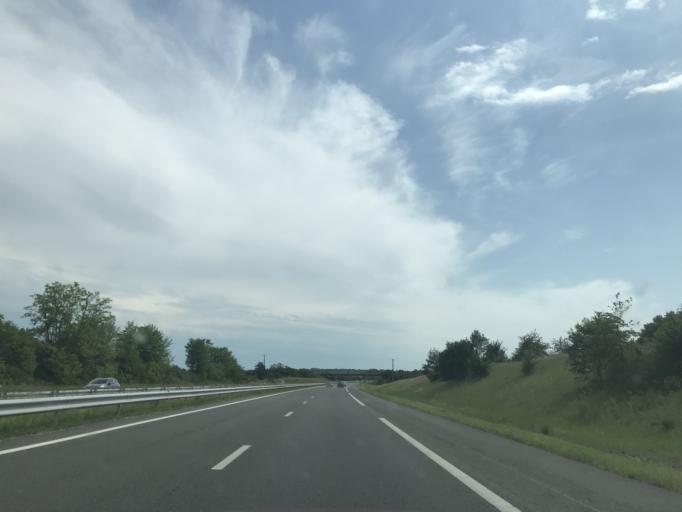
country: FR
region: Centre
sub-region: Departement du Cher
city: Orval
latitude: 46.7979
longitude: 2.4120
